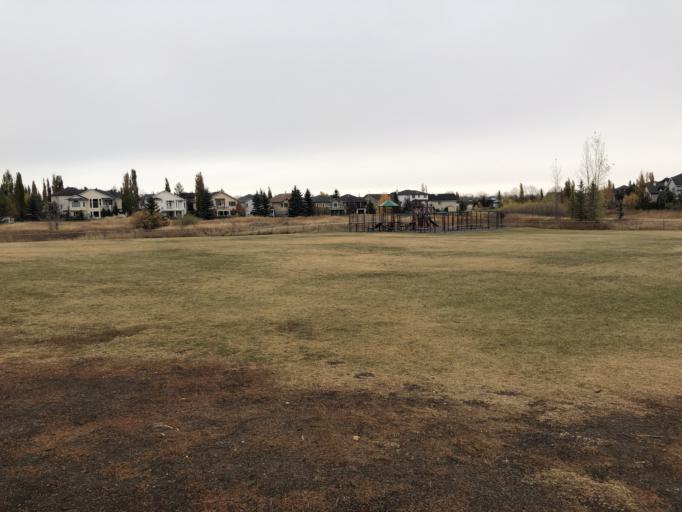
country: CA
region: Alberta
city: Okotoks
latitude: 50.7101
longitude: -113.9649
